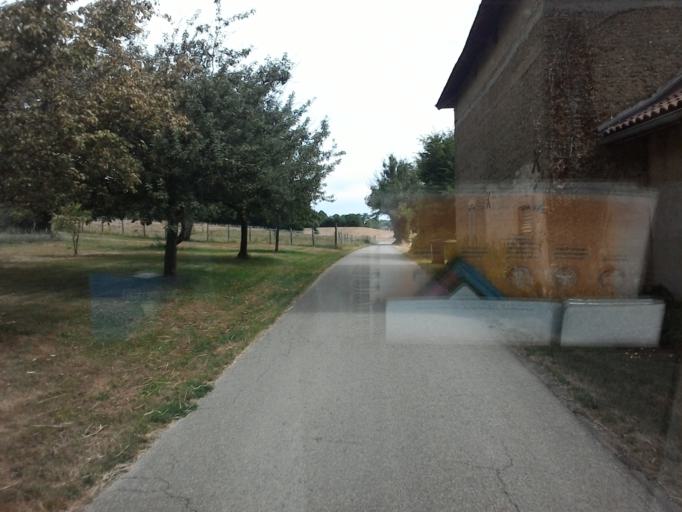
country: FR
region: Rhone-Alpes
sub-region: Departement de l'Isere
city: Montferrat
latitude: 45.4976
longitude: 5.5680
